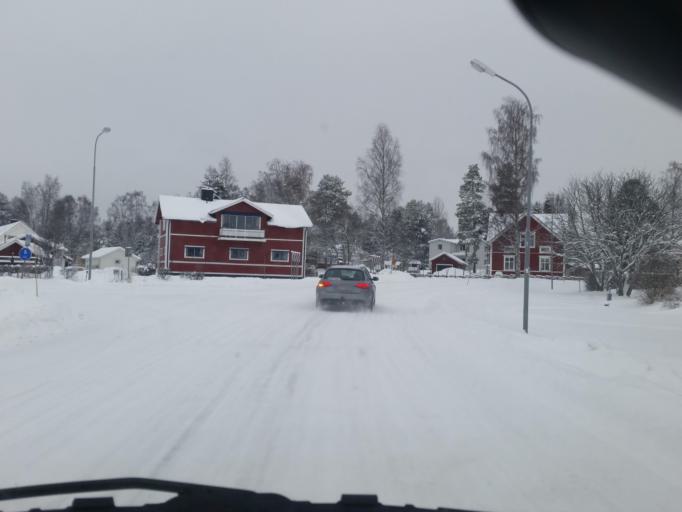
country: SE
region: Norrbotten
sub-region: Pitea Kommun
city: Bergsviken
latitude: 65.3830
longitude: 21.3140
